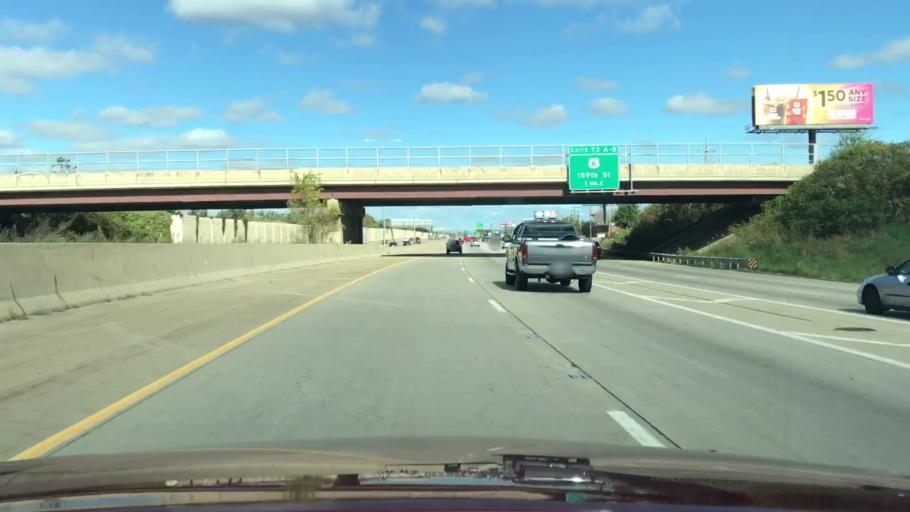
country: US
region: Illinois
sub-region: Cook County
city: South Holland
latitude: 41.5858
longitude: -87.5835
